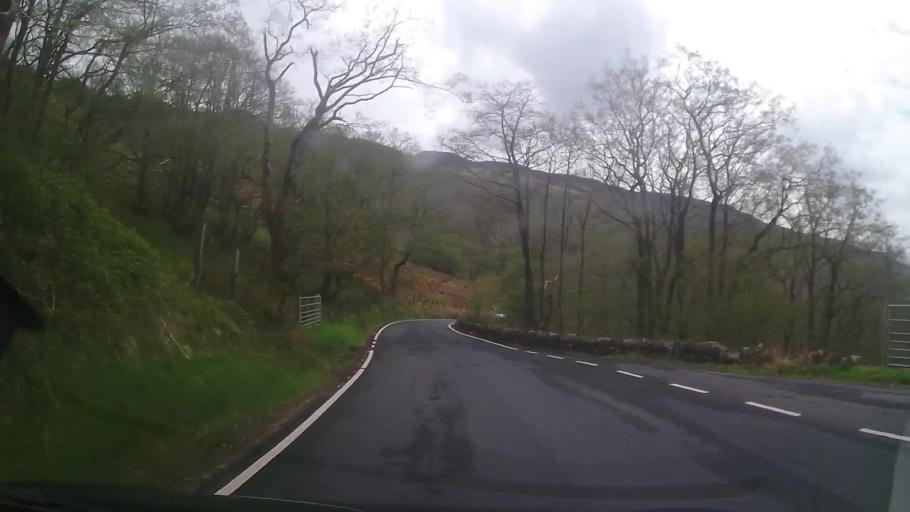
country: GB
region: Wales
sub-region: Gwynedd
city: Blaenau-Ffestiniog
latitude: 53.0573
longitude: -4.0034
